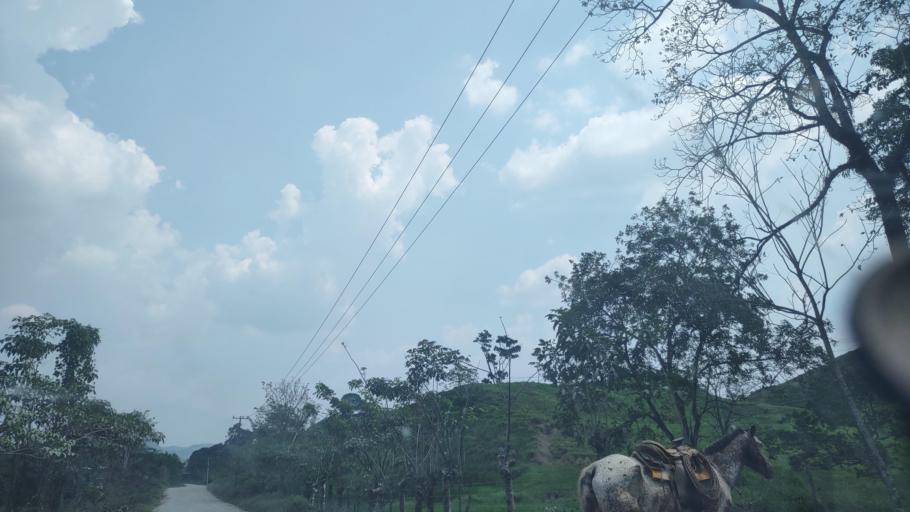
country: MX
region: Tabasco
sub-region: Huimanguillo
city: Francisco Rueda
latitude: 17.5966
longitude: -93.8997
